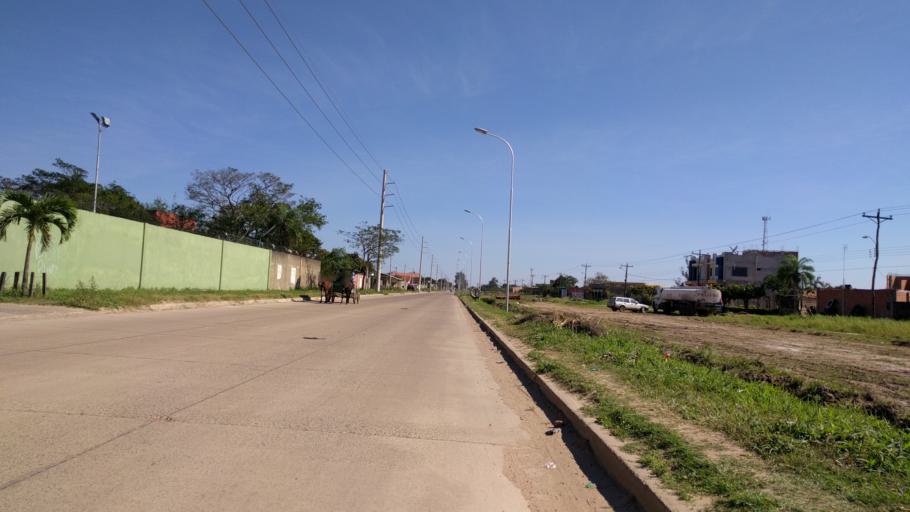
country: BO
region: Santa Cruz
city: Santa Cruz de la Sierra
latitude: -17.8718
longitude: -63.1944
